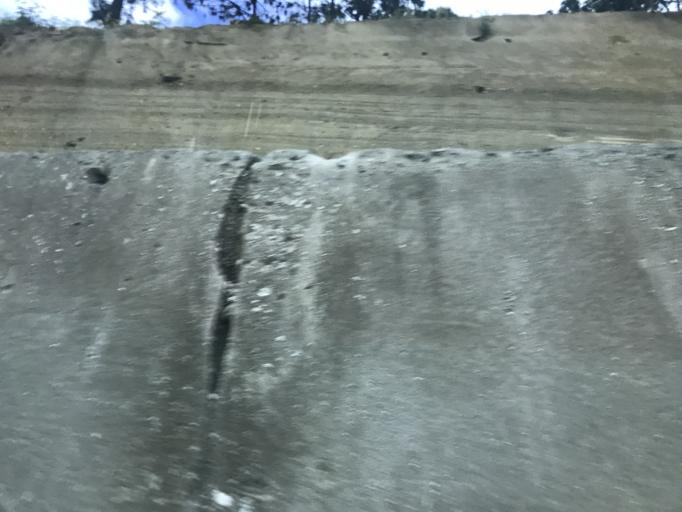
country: GT
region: Chimaltenango
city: Parramos
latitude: 14.6260
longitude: -90.7985
